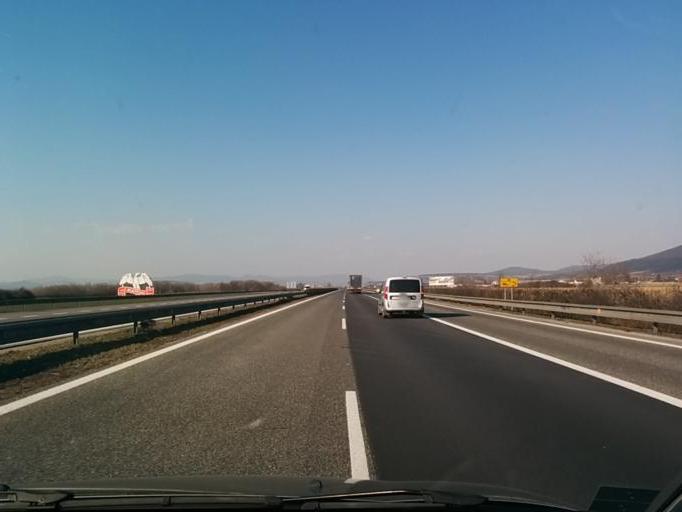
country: SK
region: Trenciansky
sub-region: Okres Nove Mesto nad Vahom
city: Nove Mesto nad Vahom
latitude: 48.7096
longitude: 17.8727
